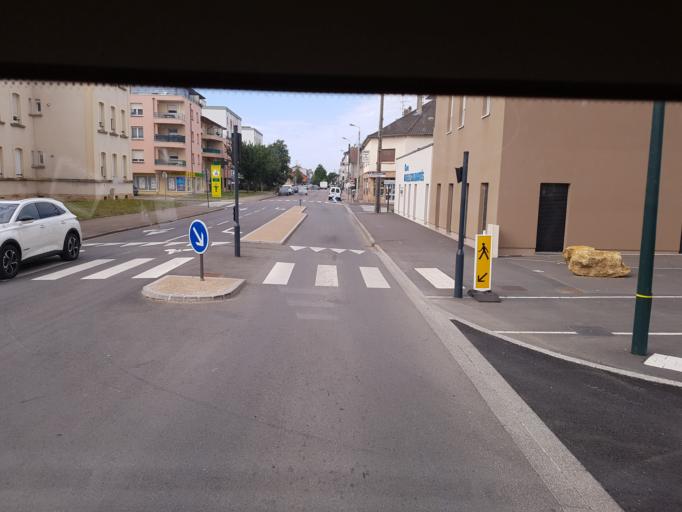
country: FR
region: Lorraine
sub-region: Departement de la Moselle
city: Yutz
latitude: 49.3628
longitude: 6.1988
